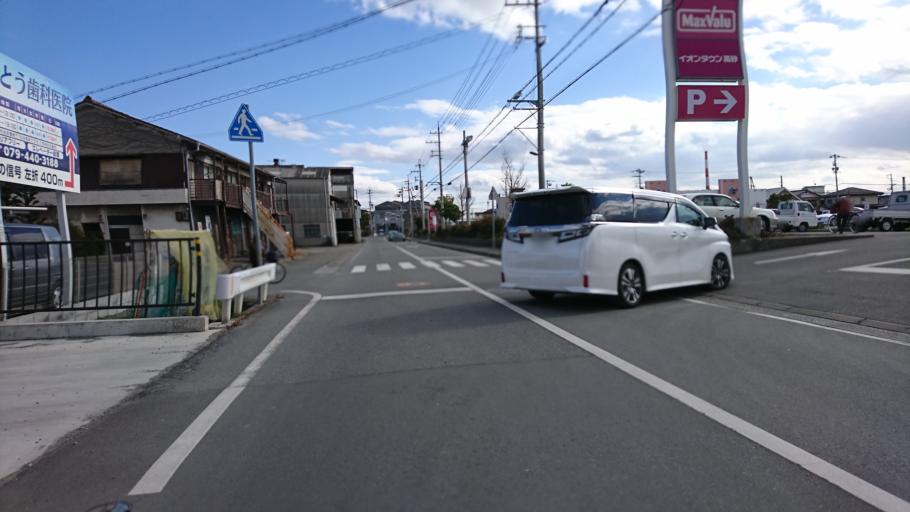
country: JP
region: Hyogo
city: Kakogawacho-honmachi
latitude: 34.7655
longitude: 134.7772
